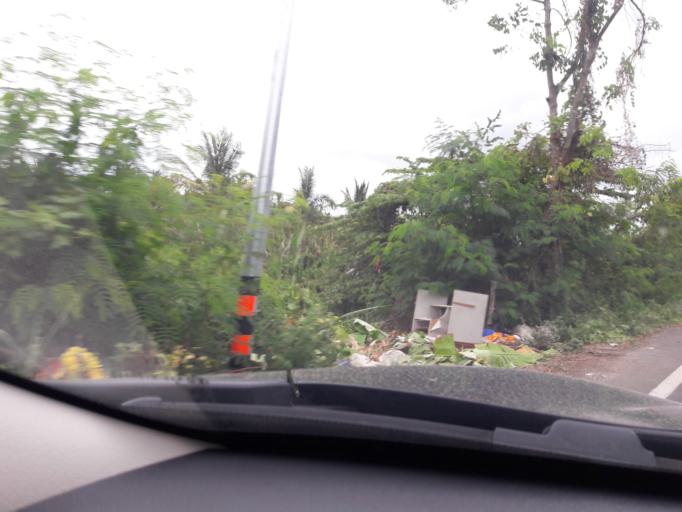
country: TH
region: Ratchaburi
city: Damnoen Saduak
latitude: 13.5981
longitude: 99.9437
